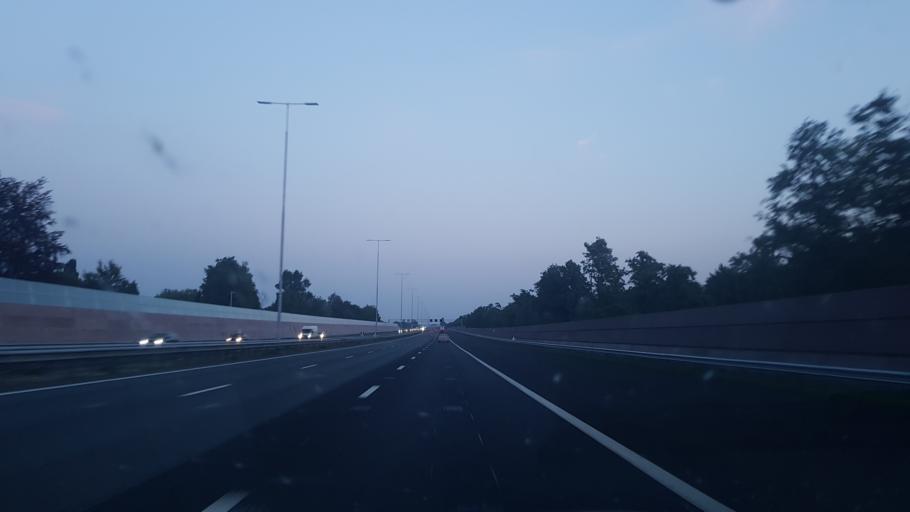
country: NL
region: North Holland
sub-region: Gemeente Wijdemeren
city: Nieuw-Loosdrecht
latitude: 52.1757
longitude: 5.1784
